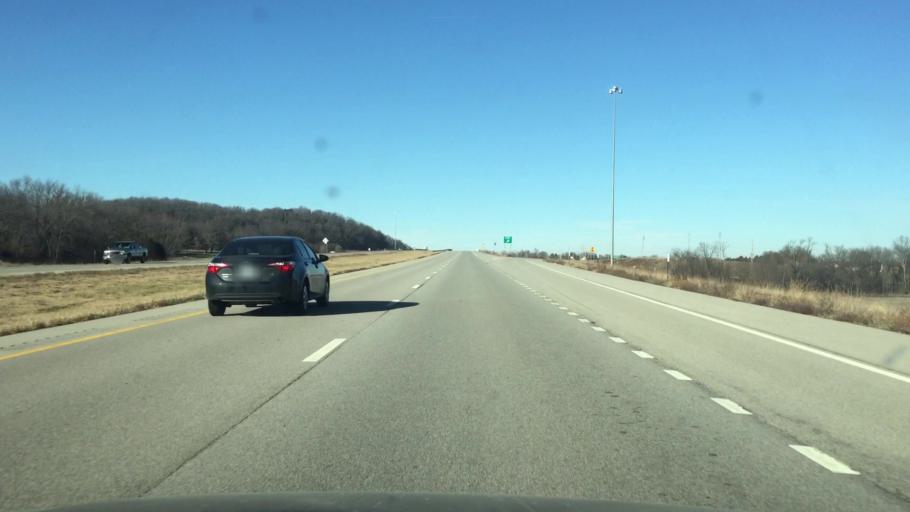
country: US
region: Kansas
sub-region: Douglas County
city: Lawrence
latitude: 38.8809
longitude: -95.2572
